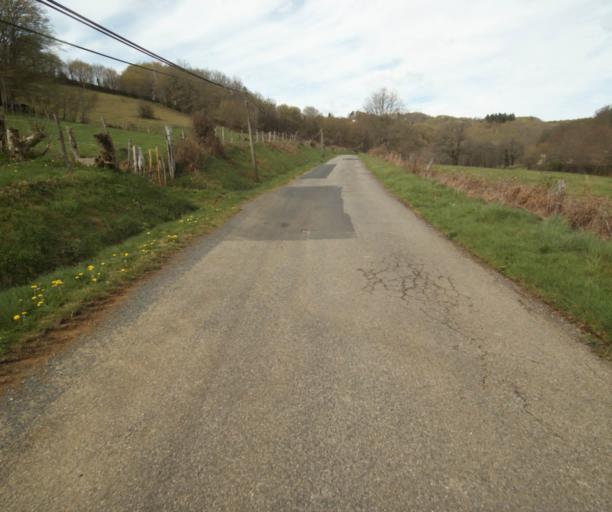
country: FR
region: Limousin
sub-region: Departement de la Correze
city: Laguenne
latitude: 45.2339
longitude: 1.8504
